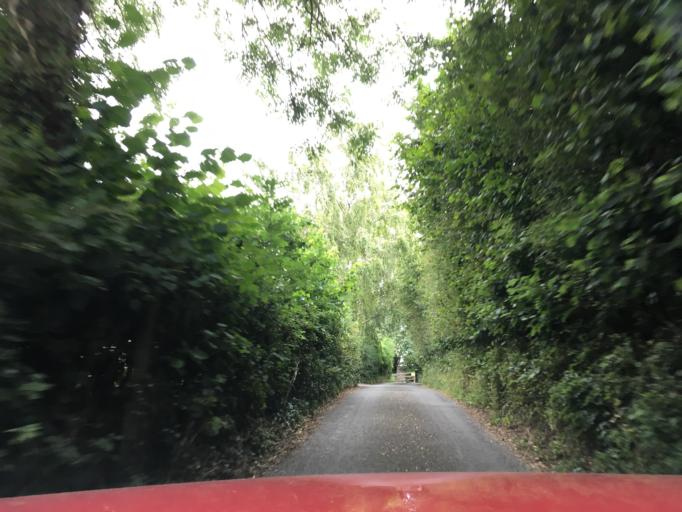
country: GB
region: England
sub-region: Kent
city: Maidstone
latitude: 51.2374
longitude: 0.5410
